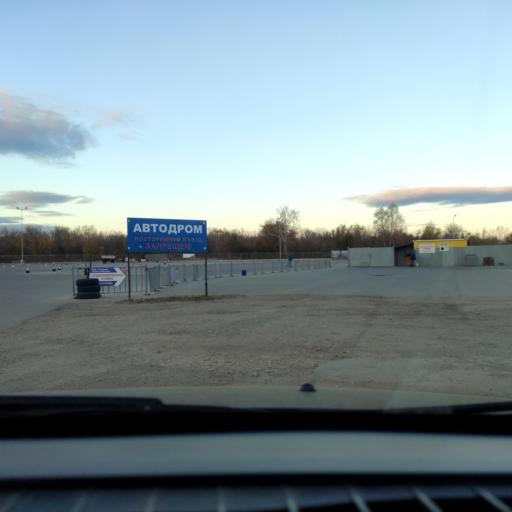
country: RU
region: Samara
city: Tol'yatti
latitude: 53.5457
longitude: 49.2744
